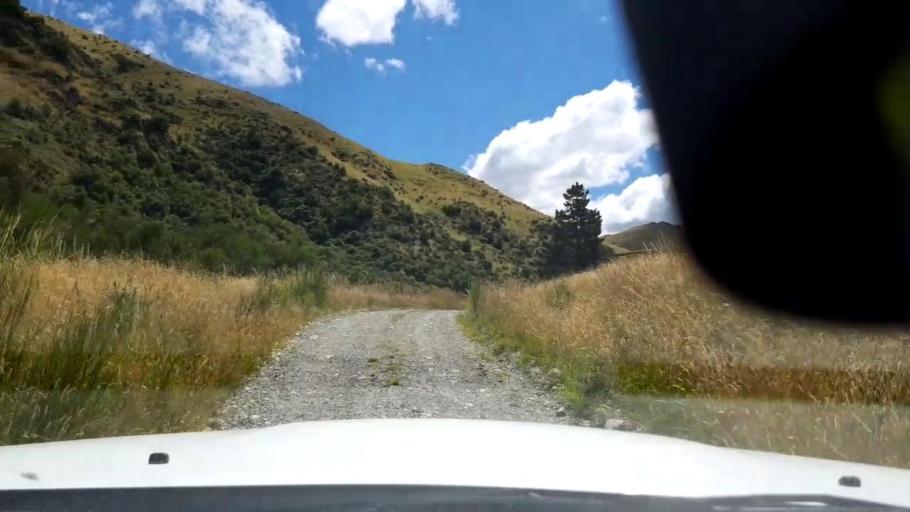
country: NZ
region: Canterbury
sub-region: Timaru District
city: Pleasant Point
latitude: -43.9299
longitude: 171.1921
